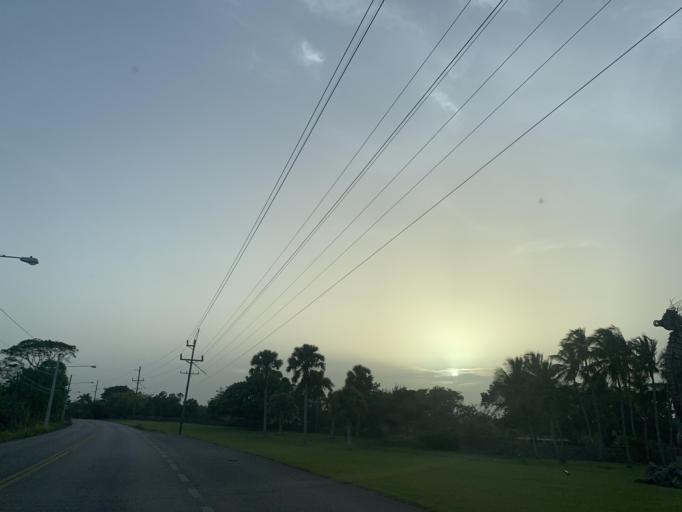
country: DO
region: Puerto Plata
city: Cabarete
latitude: 19.7788
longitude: -70.4822
